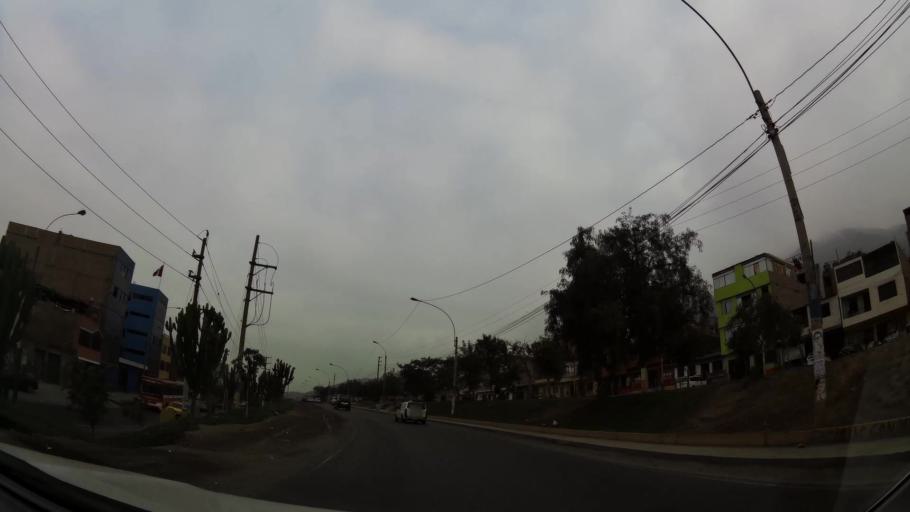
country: PE
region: Lima
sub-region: Lima
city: Independencia
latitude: -11.9926
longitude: -77.0153
